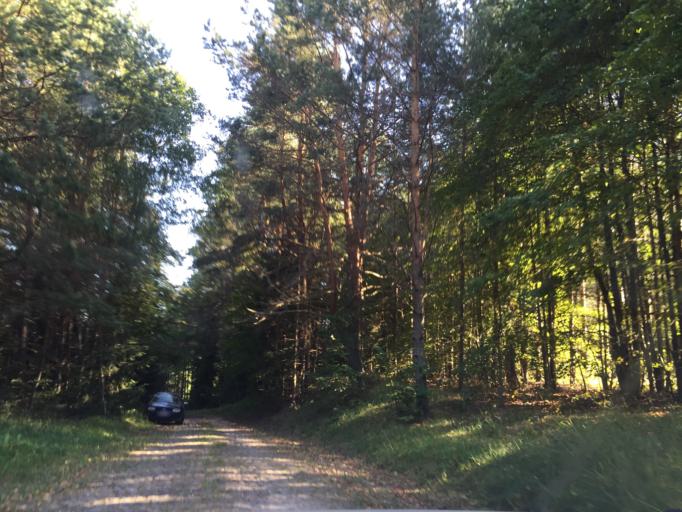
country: LT
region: Panevezys
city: Rokiskis
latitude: 55.8232
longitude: 25.8968
